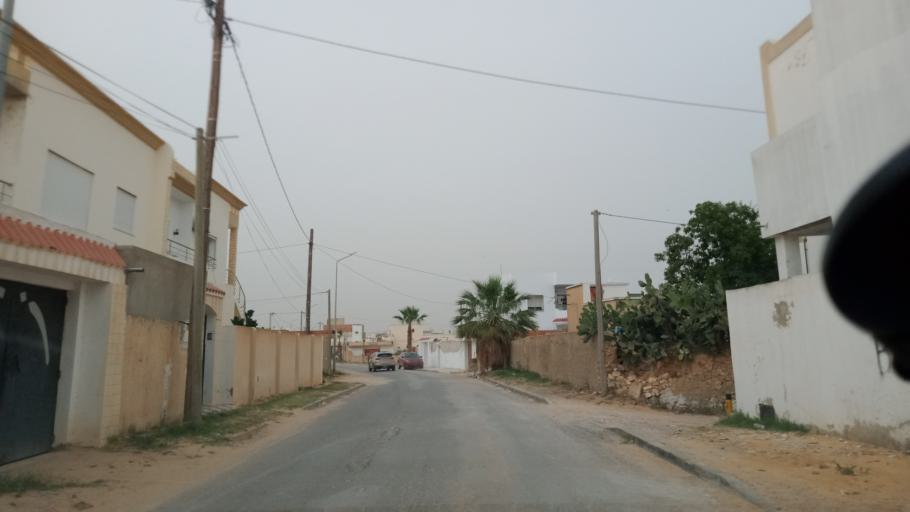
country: TN
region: Safaqis
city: Al Qarmadah
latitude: 34.7945
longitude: 10.7711
